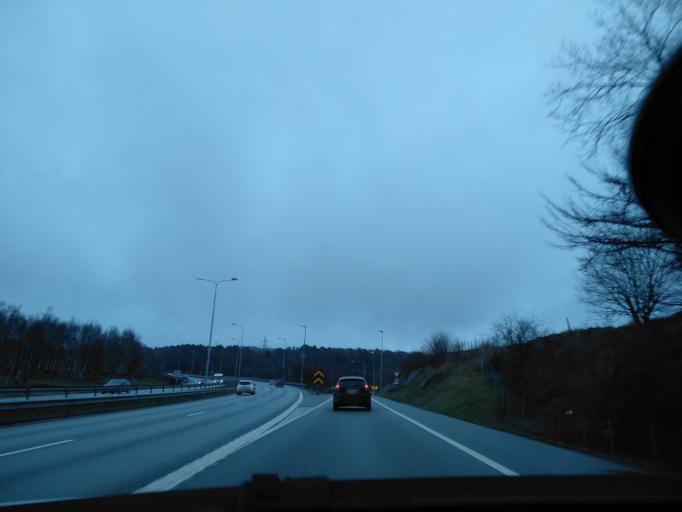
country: NO
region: Rogaland
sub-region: Stavanger
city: Stavanger
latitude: 58.9203
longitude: 5.7049
